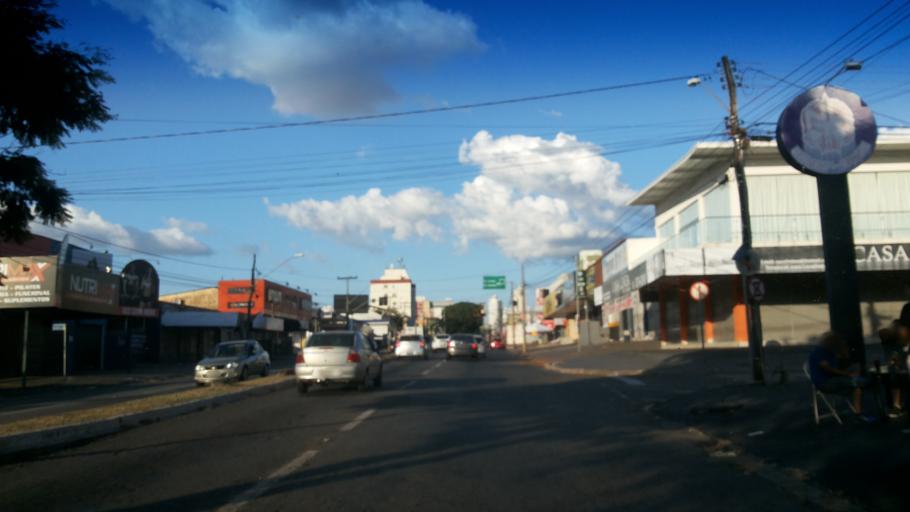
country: BR
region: Goias
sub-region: Goiania
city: Goiania
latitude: -16.7097
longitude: -49.2927
